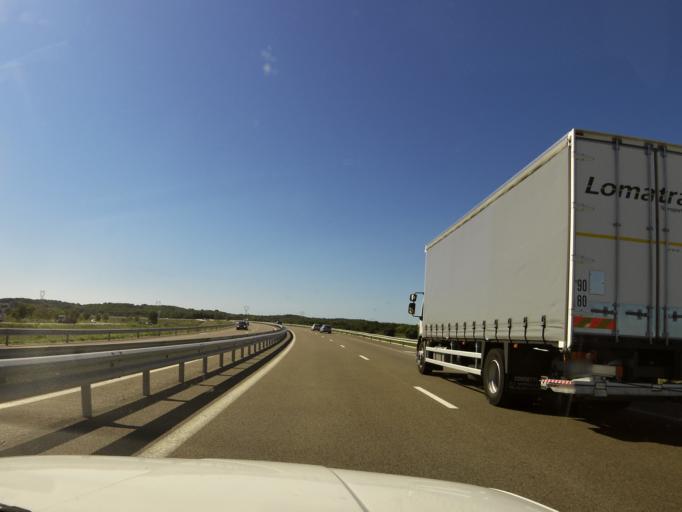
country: FR
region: Languedoc-Roussillon
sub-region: Departement du Gard
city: La Calmette
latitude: 43.9274
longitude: 4.2545
